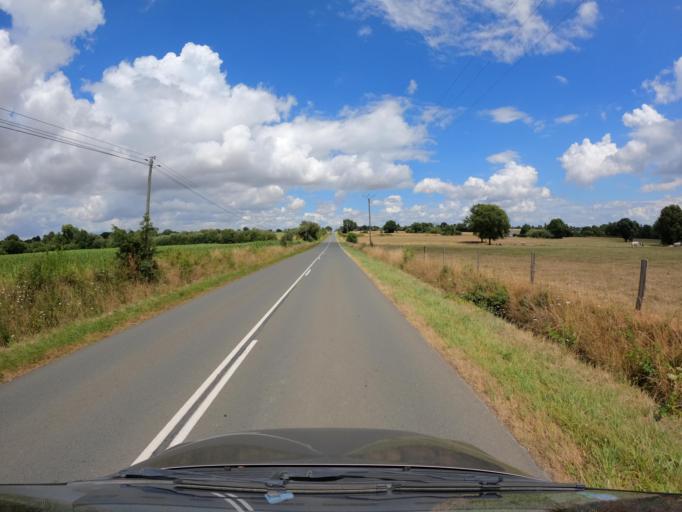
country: FR
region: Pays de la Loire
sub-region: Departement de Maine-et-Loire
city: Chateauneuf-sur-Sarthe
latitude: 47.7137
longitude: -0.5309
